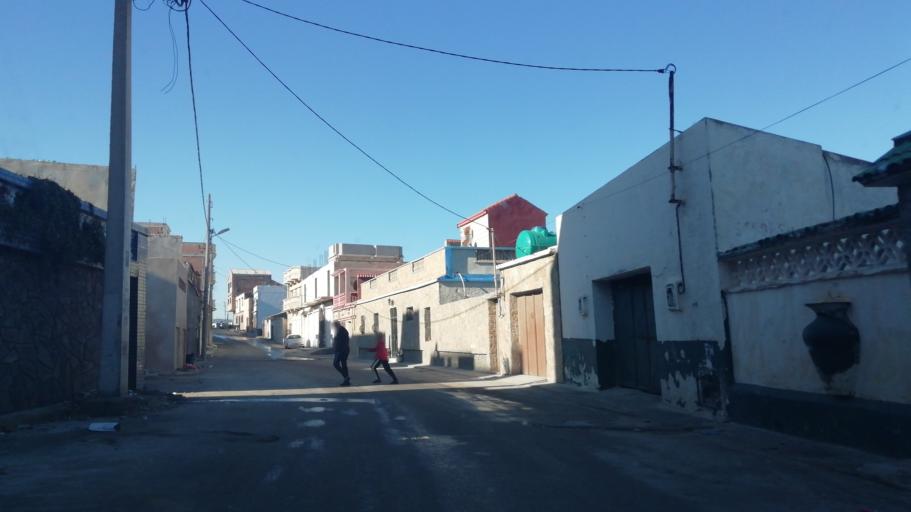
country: DZ
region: Oran
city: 'Ain el Turk
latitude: 35.7272
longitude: -0.8470
